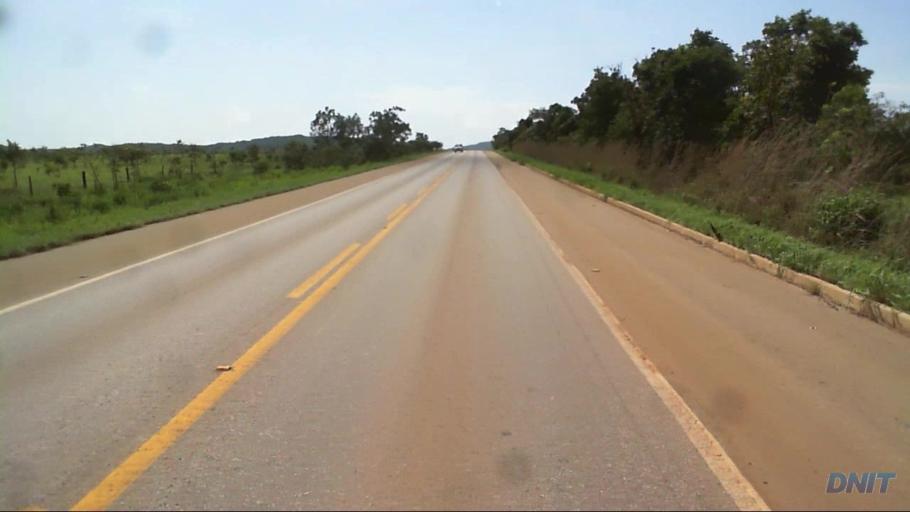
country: BR
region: Goias
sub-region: Barro Alto
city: Barro Alto
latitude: -15.1865
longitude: -48.7803
